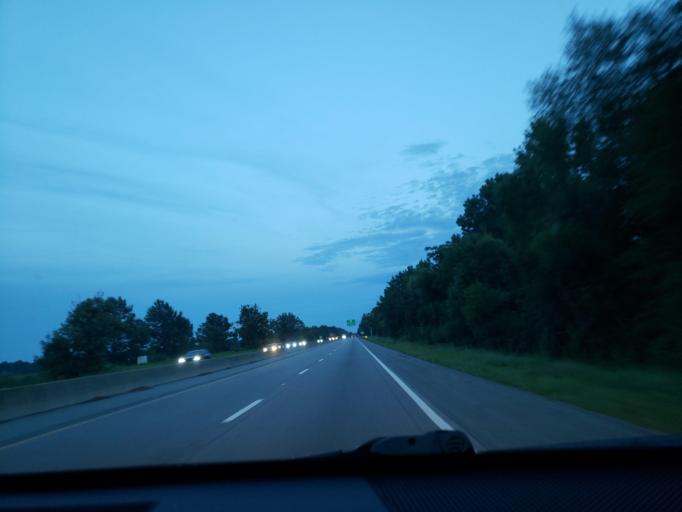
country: US
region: Virginia
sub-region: City of Franklin
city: Franklin
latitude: 36.6551
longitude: -76.9269
